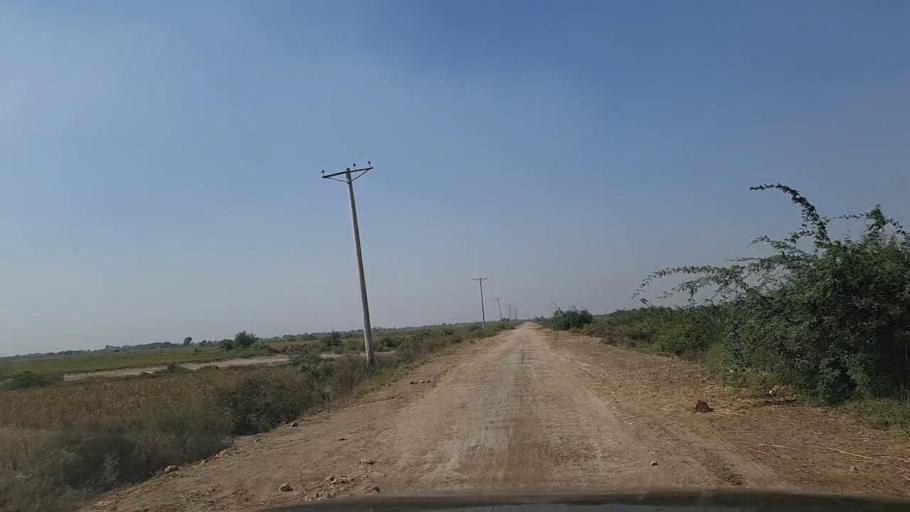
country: PK
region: Sindh
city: Daro Mehar
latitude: 24.8334
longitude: 68.1713
